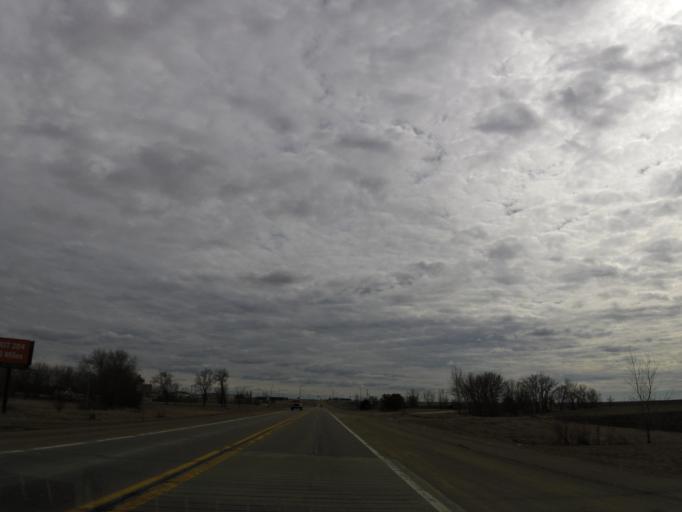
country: US
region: Iowa
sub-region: Howard County
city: Cresco
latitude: 43.3737
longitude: -92.2983
